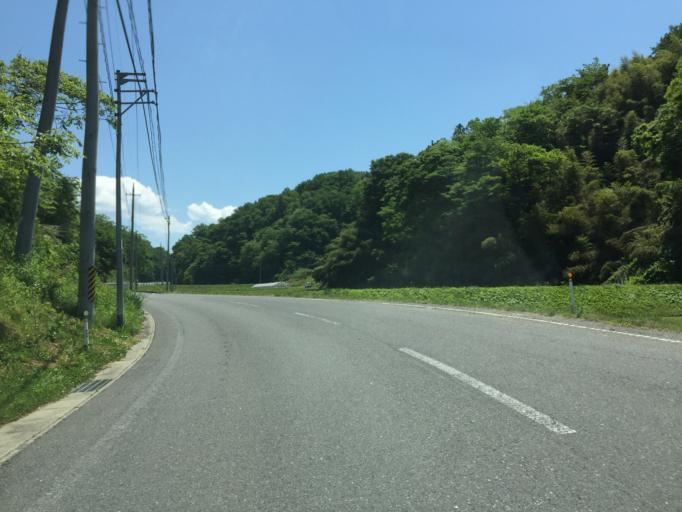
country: JP
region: Fukushima
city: Funehikimachi-funehiki
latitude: 37.4870
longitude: 140.5520
